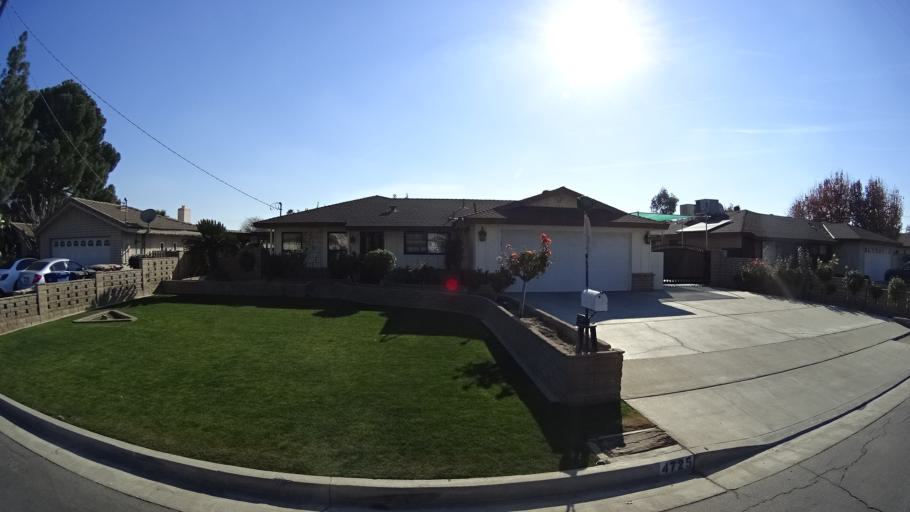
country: US
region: California
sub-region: Kern County
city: Greenfield
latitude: 35.3047
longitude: -119.0554
